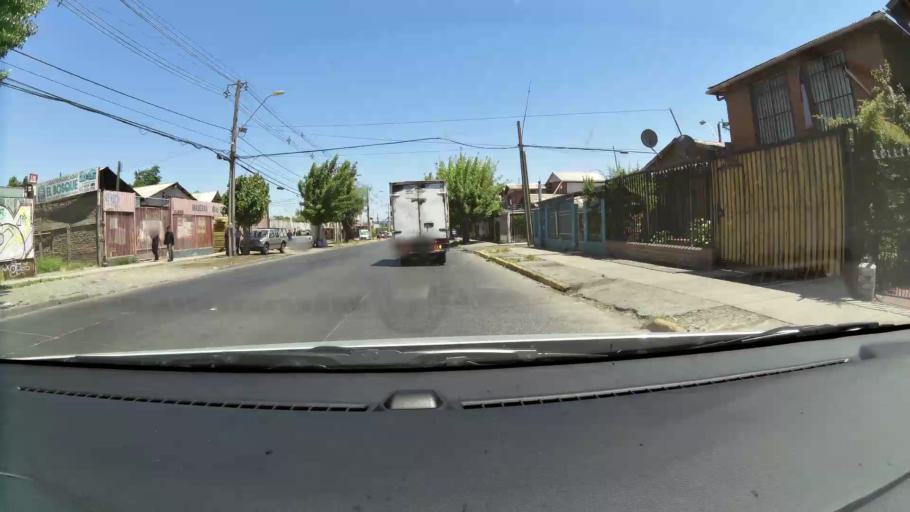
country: CL
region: Santiago Metropolitan
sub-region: Provincia de Santiago
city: La Pintana
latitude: -33.5736
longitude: -70.6610
